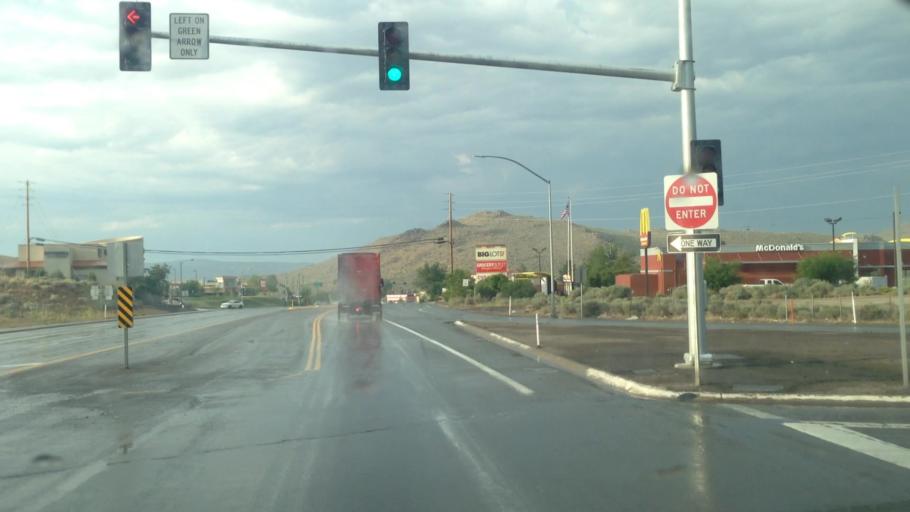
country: US
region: Nevada
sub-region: Washoe County
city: Golden Valley
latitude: 39.6116
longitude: -119.8505
